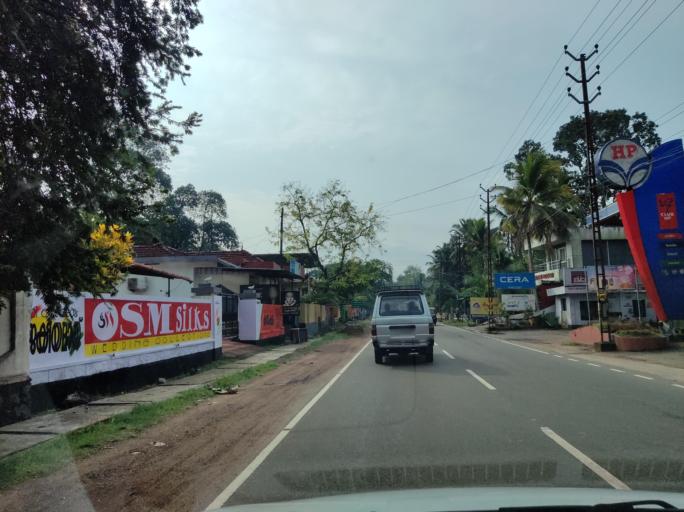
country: IN
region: Kerala
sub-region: Alappuzha
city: Kattanam
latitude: 9.1728
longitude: 76.5934
